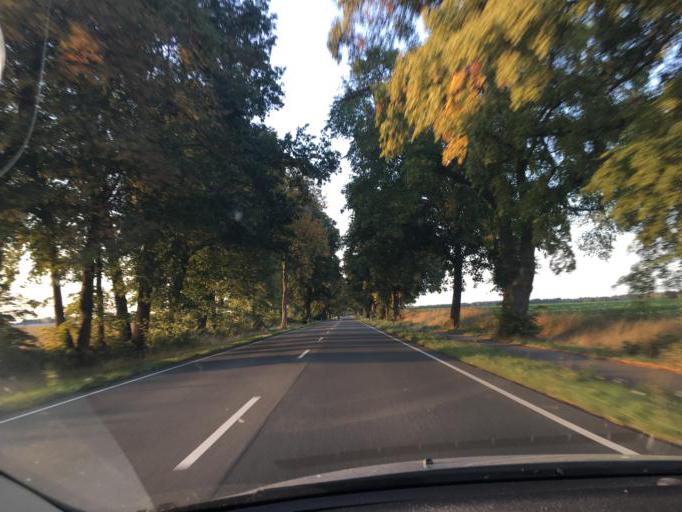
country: DE
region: Lower Saxony
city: Bergen
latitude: 52.8541
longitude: 9.9123
